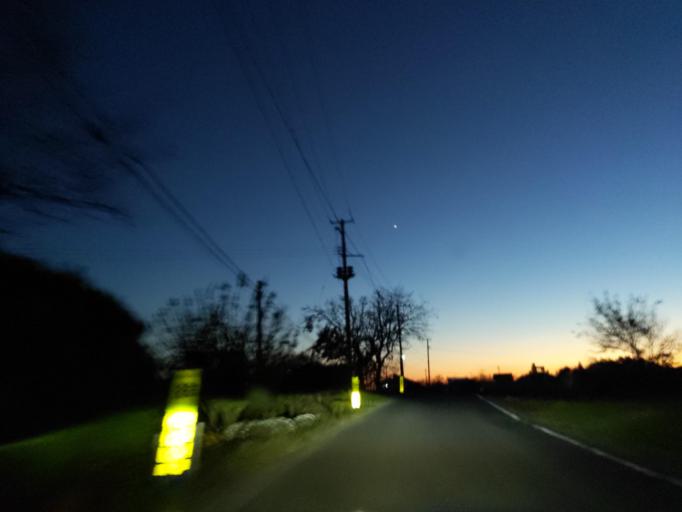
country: JP
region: Fukushima
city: Sukagawa
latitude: 37.3185
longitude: 140.3906
